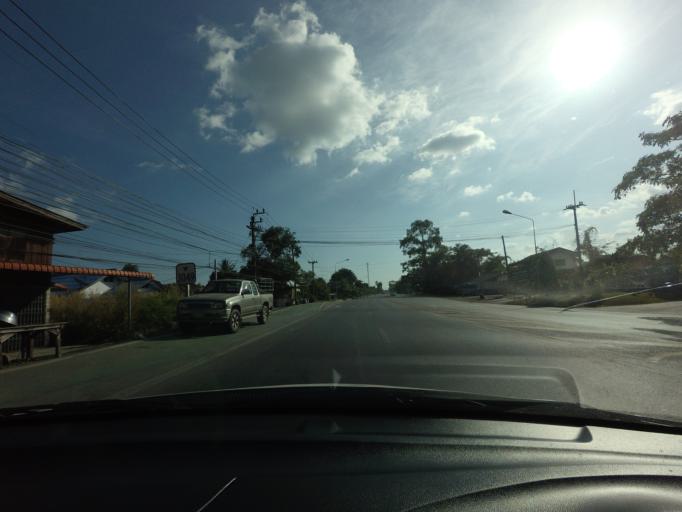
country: TH
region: Nakhon Nayok
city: Nakhon Nayok
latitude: 14.2841
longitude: 101.2764
